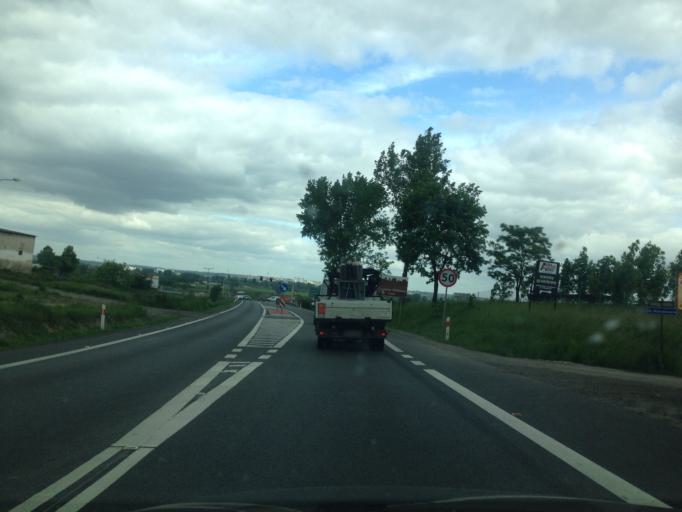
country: PL
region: Kujawsko-Pomorskie
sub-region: Powiat chelminski
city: Chelmno
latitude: 53.3503
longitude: 18.4521
